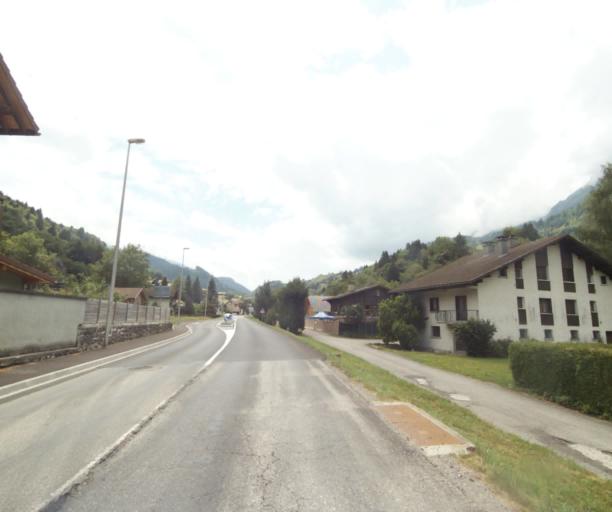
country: FR
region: Rhone-Alpes
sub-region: Departement de la Haute-Savoie
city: Thones
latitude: 45.8714
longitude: 6.3233
